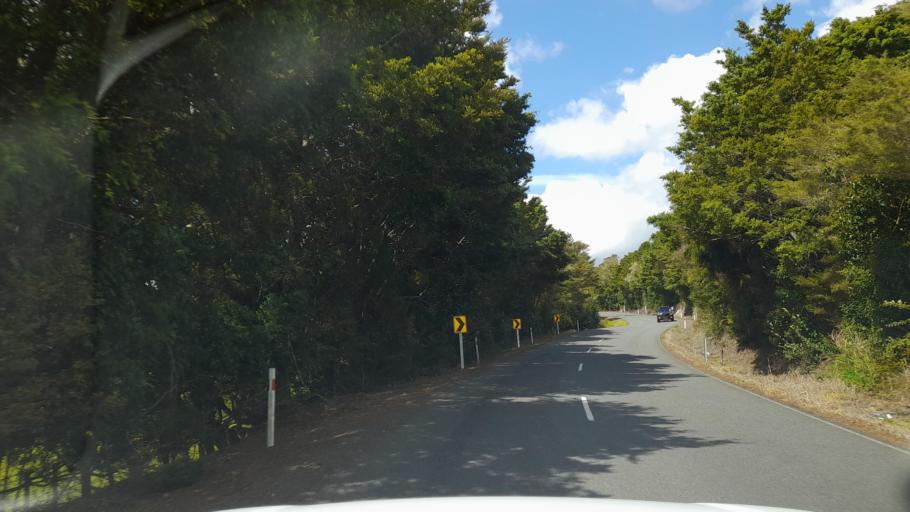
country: NZ
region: Northland
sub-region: Whangarei
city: Maungatapere
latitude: -35.6388
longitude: 174.0650
